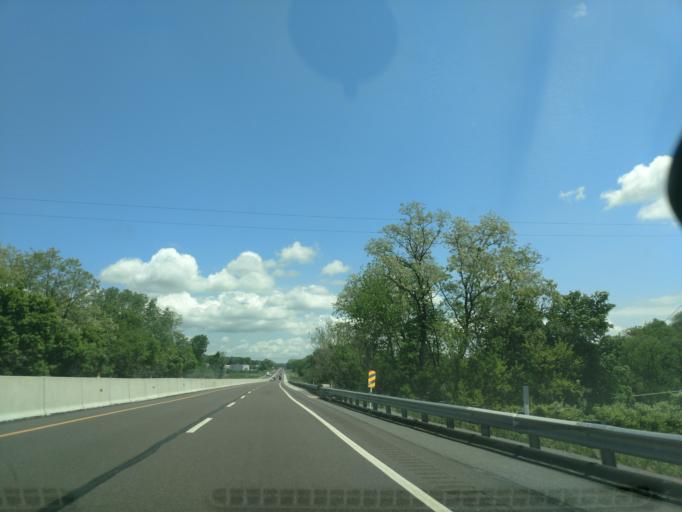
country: US
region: Pennsylvania
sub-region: Lancaster County
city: Schoeneck
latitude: 40.2459
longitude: -76.2152
